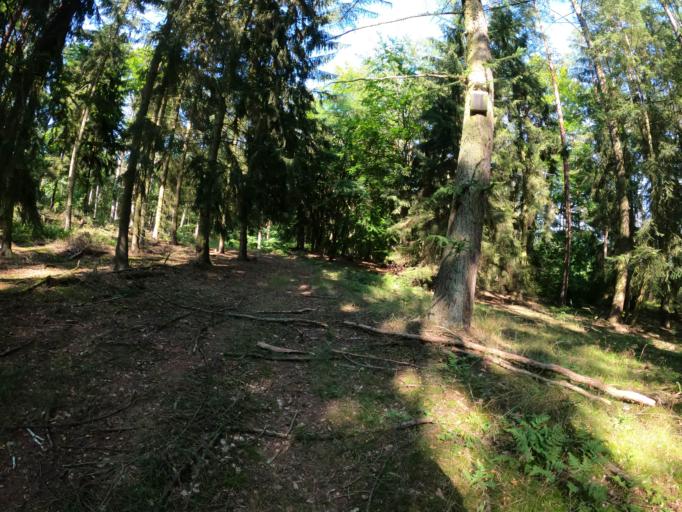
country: DE
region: Brandenburg
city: Angermunde
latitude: 53.0262
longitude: 13.9185
